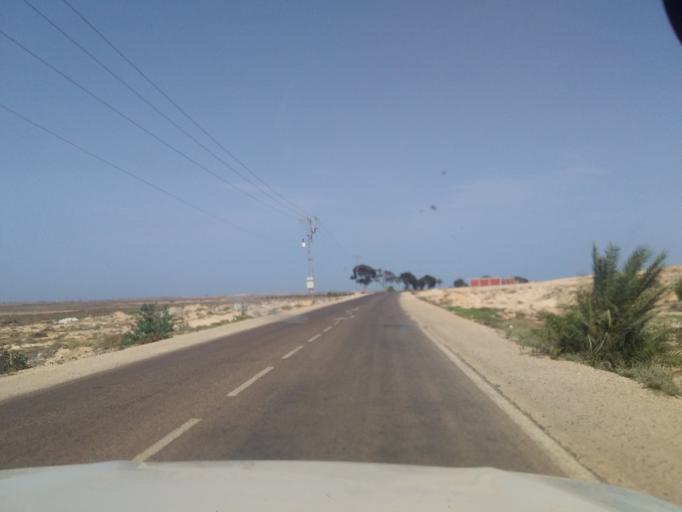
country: TN
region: Qabis
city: Gabes
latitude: 33.6385
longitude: 10.2858
